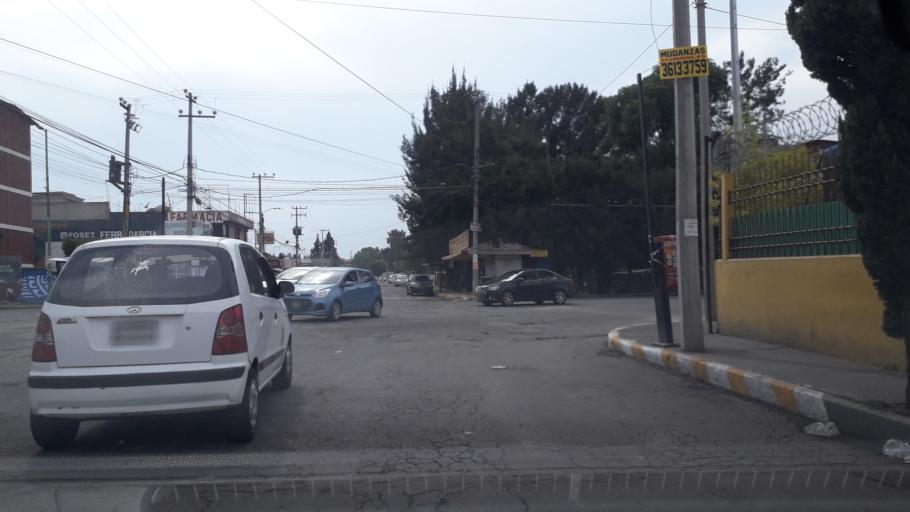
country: MX
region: Mexico
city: Coacalco
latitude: 19.6378
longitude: -99.0787
